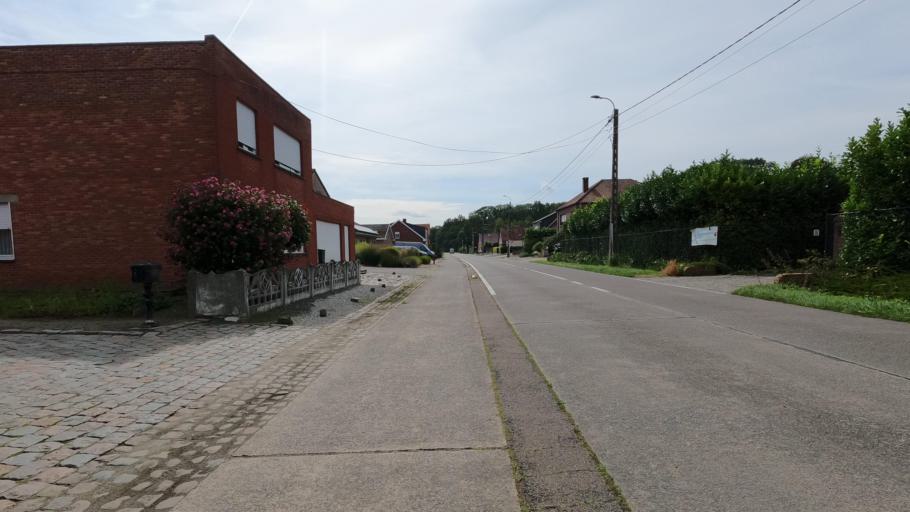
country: BE
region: Flanders
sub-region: Provincie Antwerpen
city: Berlaar
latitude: 51.1128
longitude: 4.7022
